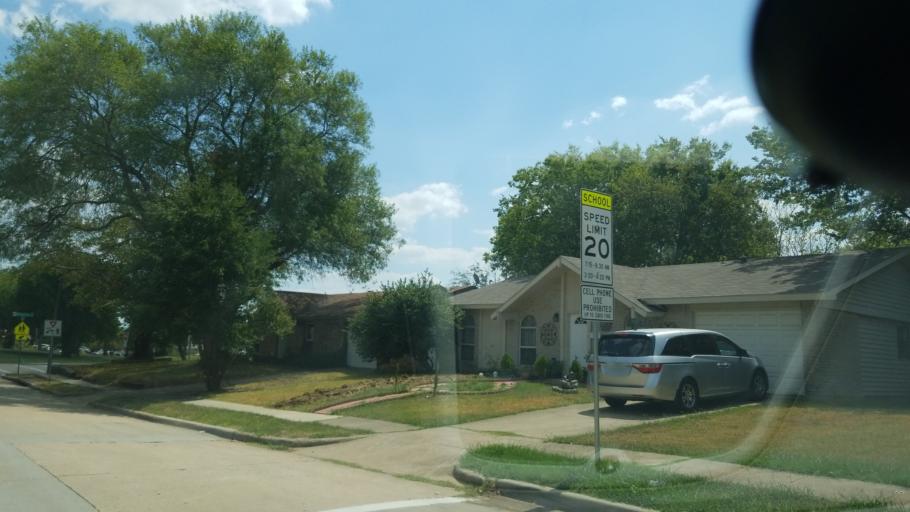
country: US
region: Texas
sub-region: Dallas County
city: Grand Prairie
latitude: 32.7039
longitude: -96.9906
